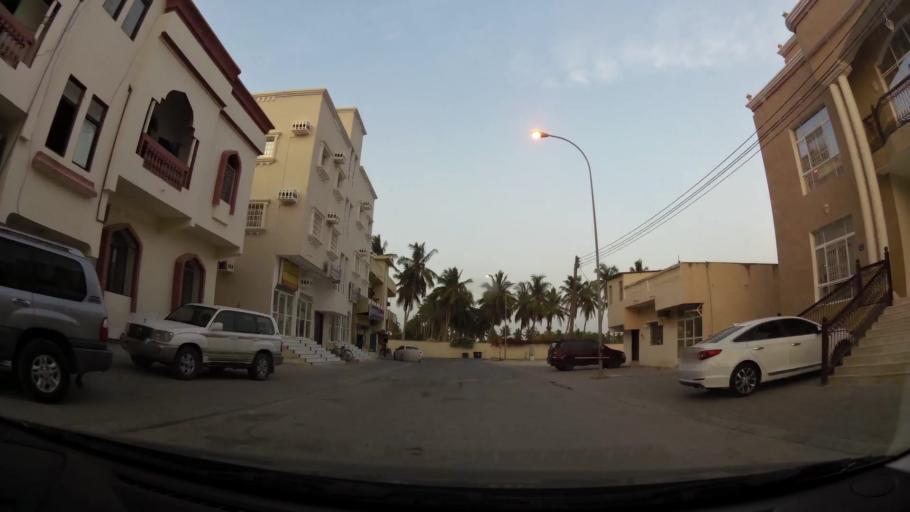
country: OM
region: Zufar
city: Salalah
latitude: 17.0214
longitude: 54.1282
